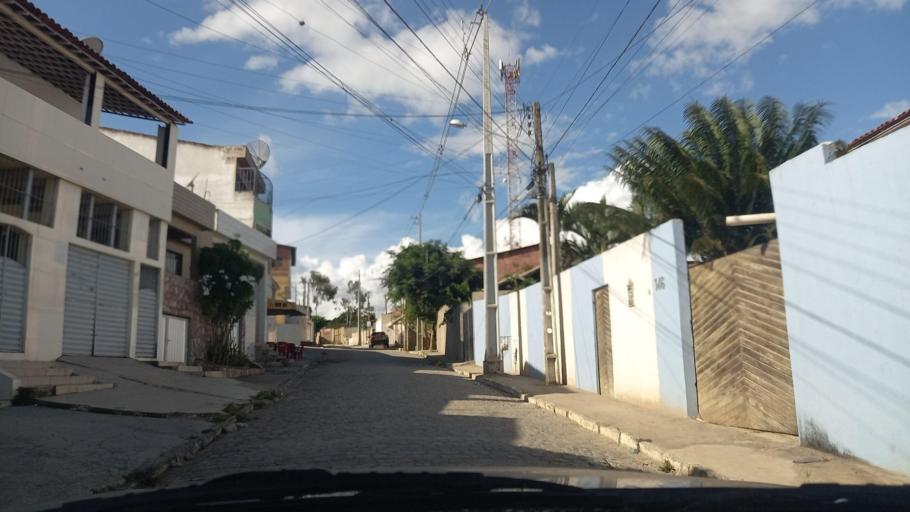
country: BR
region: Pernambuco
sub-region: Gravata
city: Gravata
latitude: -8.1990
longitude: -35.5670
